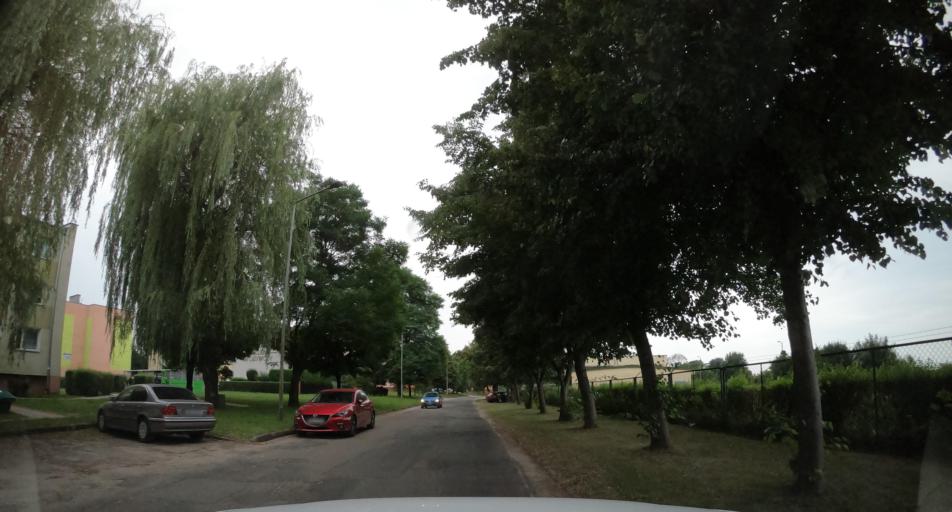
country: PL
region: West Pomeranian Voivodeship
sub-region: Powiat walecki
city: Walcz
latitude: 53.2755
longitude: 16.4525
